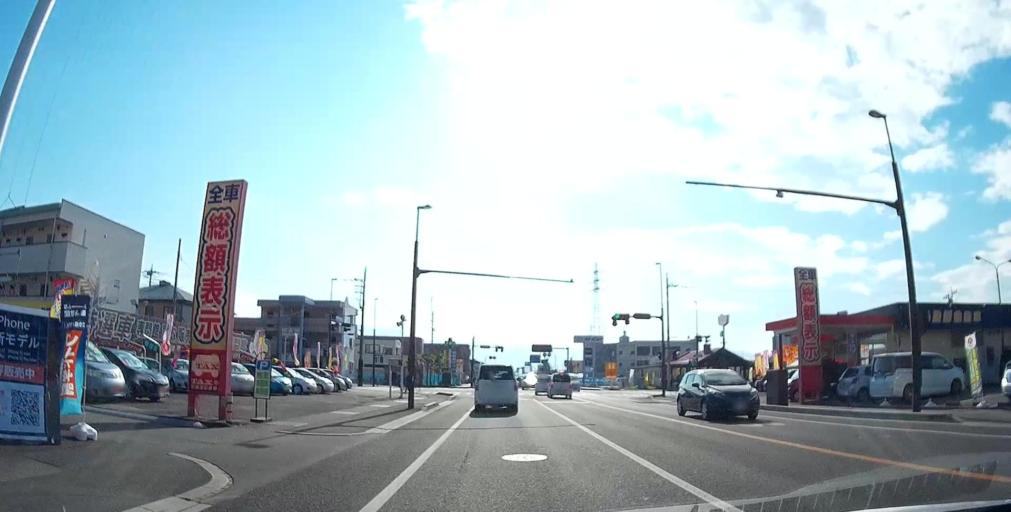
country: JP
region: Yamanashi
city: Isawa
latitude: 35.6545
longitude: 138.6140
